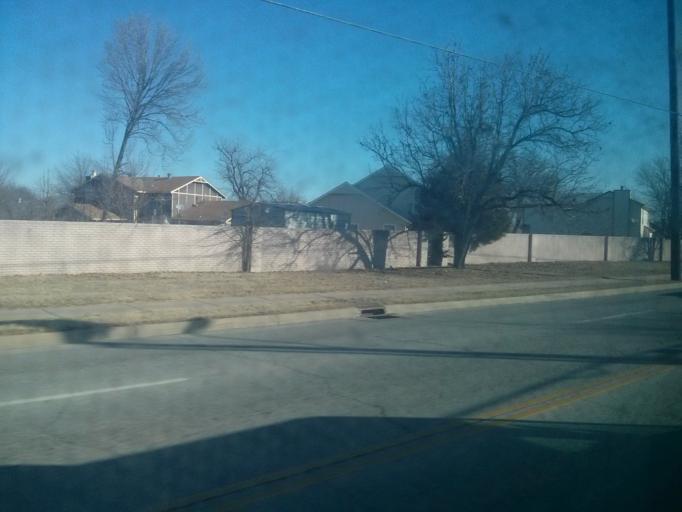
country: US
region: Oklahoma
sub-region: Tulsa County
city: Tulsa
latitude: 36.1769
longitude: -95.9887
